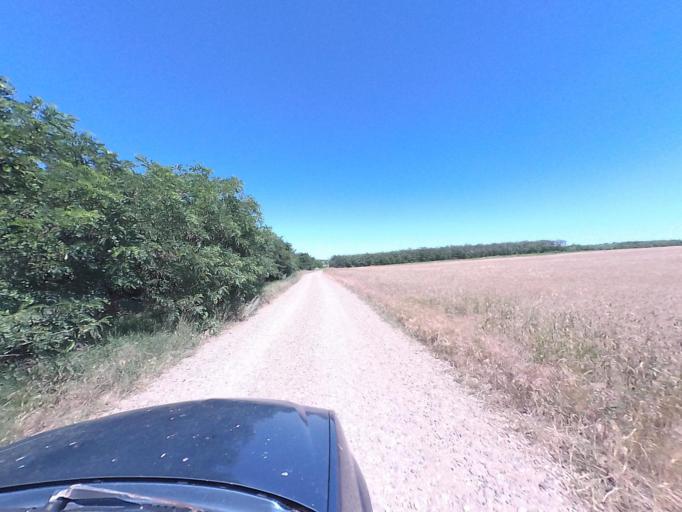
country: RO
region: Vaslui
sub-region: Comuna Costesti
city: Costesti
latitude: 46.4834
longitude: 27.7730
